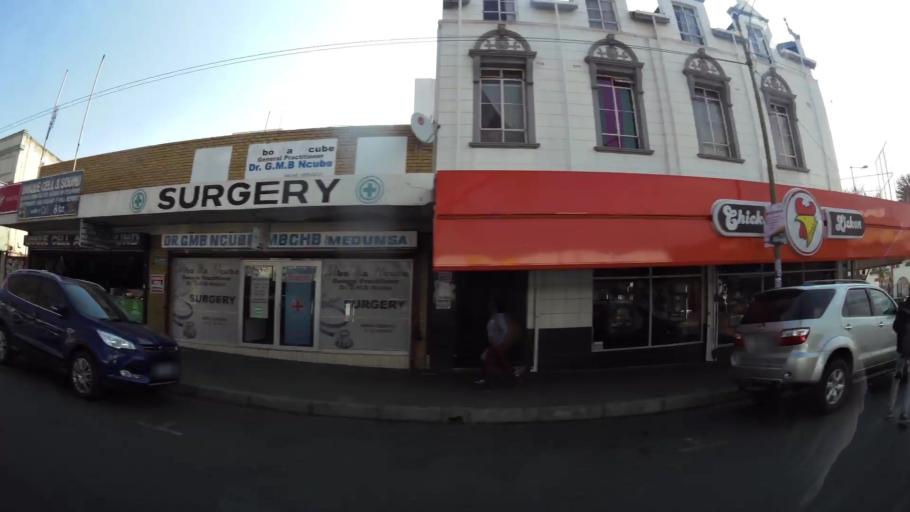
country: ZA
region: Gauteng
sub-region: West Rand District Municipality
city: Krugersdorp
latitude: -26.1023
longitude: 27.7732
